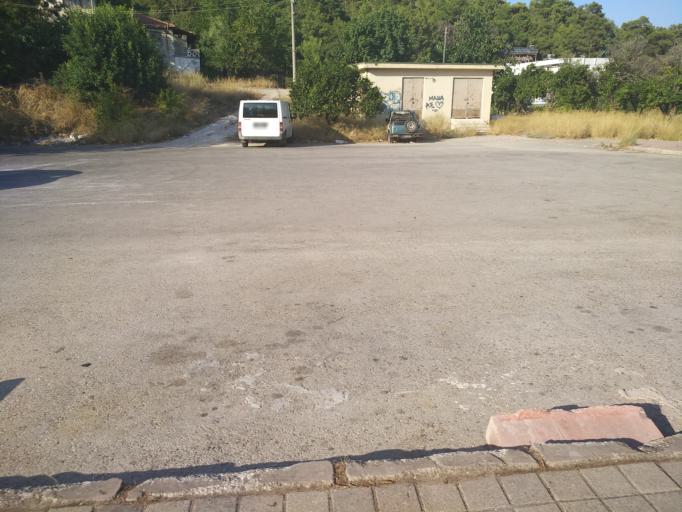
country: TR
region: Antalya
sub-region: Kemer
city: Goeynuek
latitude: 36.6665
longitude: 30.5526
